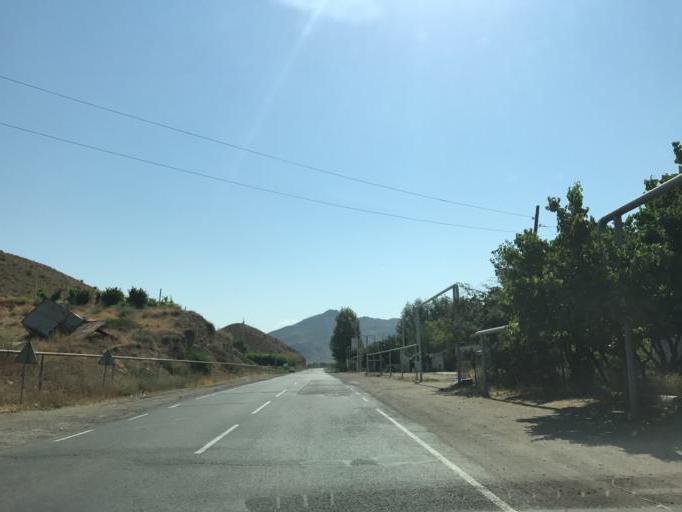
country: AM
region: Vayots' Dzori Marz
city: Getap'
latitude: 39.7363
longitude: 45.2735
